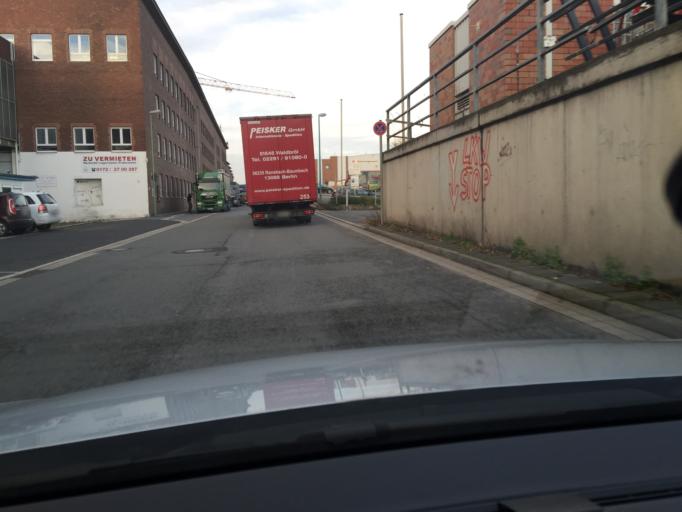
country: DE
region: North Rhine-Westphalia
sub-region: Regierungsbezirk Arnsberg
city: Hagen
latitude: 51.3699
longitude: 7.4555
